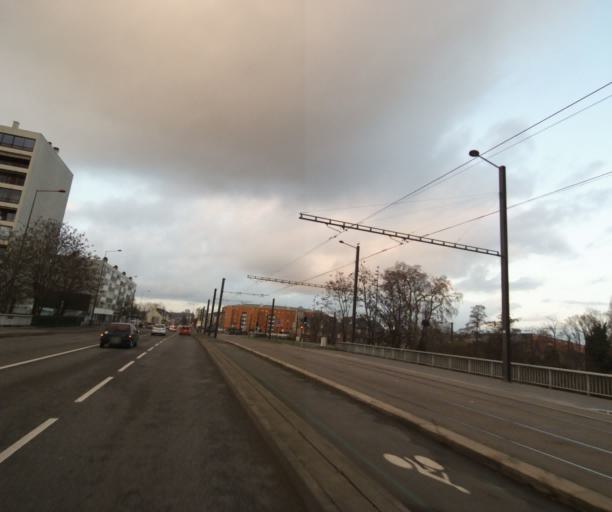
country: FR
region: Pays de la Loire
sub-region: Departement de la Sarthe
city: Le Mans
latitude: 47.9843
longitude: 0.2100
